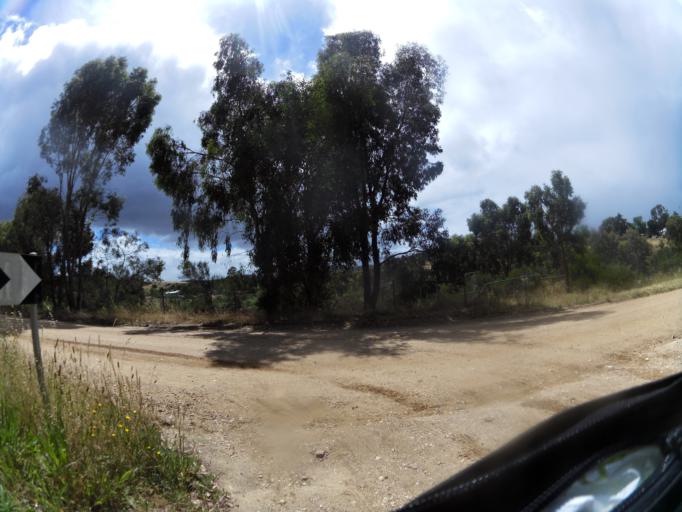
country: AU
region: Victoria
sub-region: Mount Alexander
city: Castlemaine
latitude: -37.0683
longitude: 144.2276
